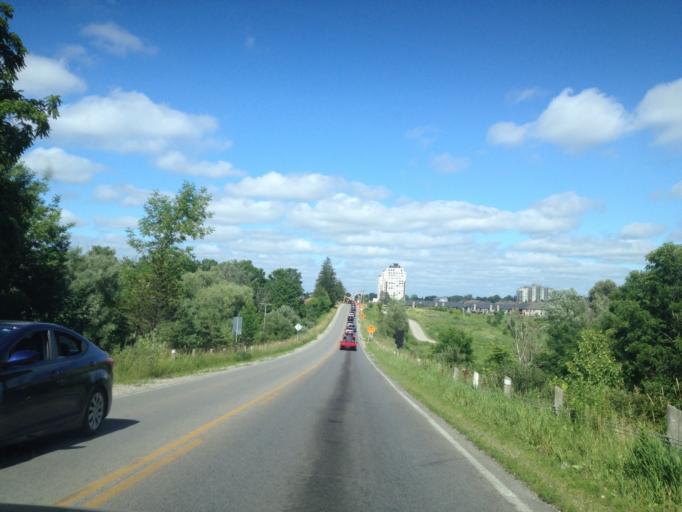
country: CA
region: Ontario
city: London
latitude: 43.0335
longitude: -81.3053
